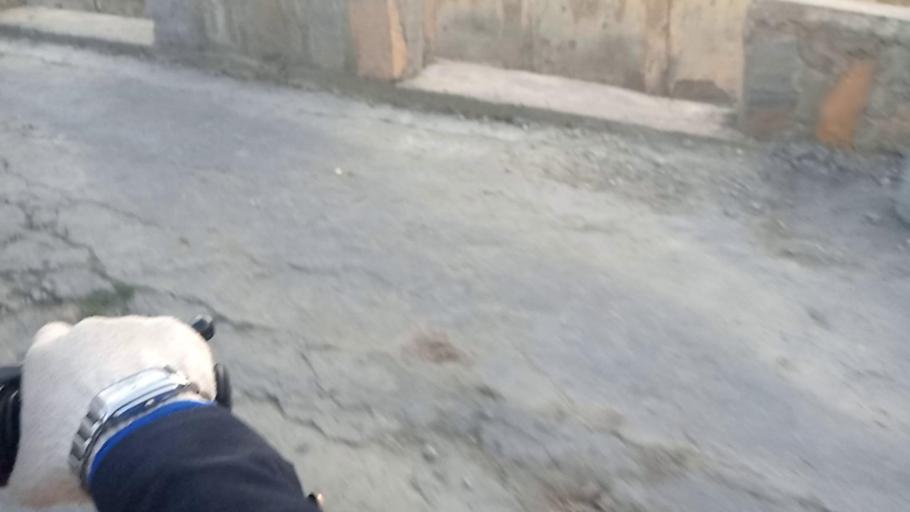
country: PK
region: Khyber Pakhtunkhwa
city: Saidu Sharif
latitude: 34.7515
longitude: 72.3589
